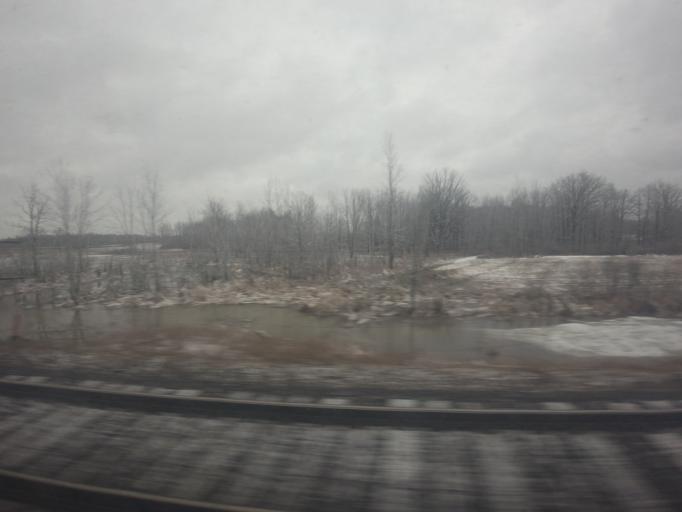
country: US
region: New York
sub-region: Jefferson County
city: Alexandria Bay
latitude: 44.4128
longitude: -76.0019
